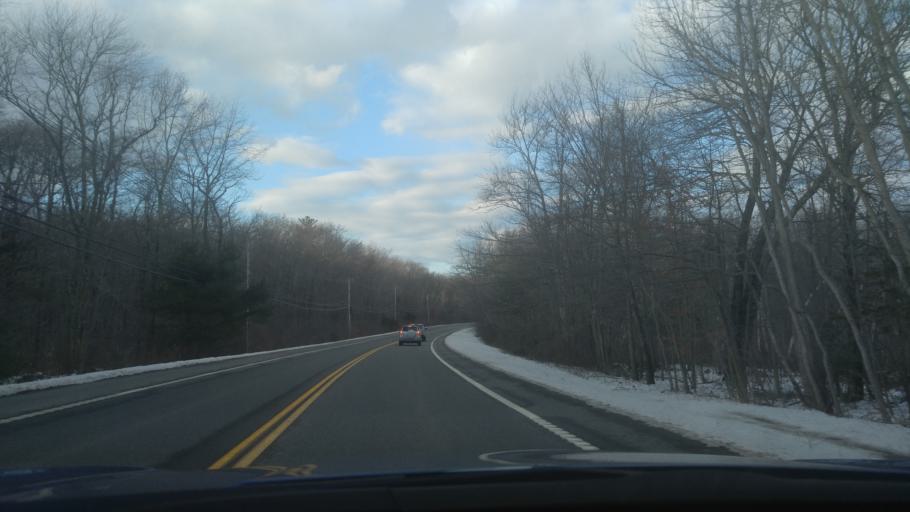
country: US
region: Rhode Island
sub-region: Kent County
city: Coventry
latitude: 41.7125
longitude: -71.7001
